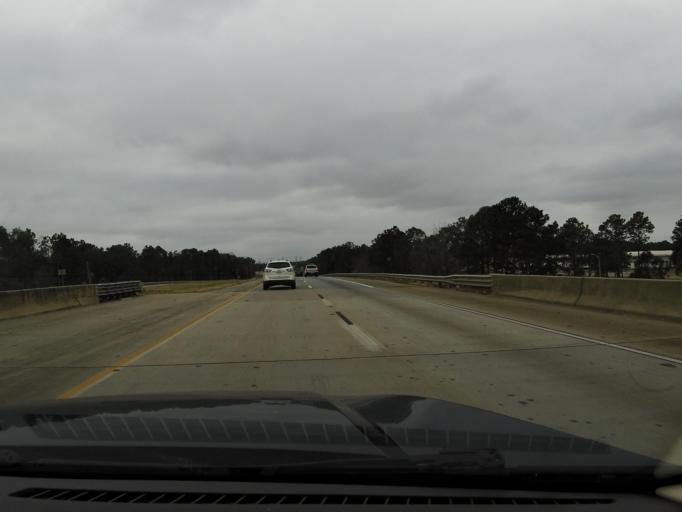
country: US
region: Georgia
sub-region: Dougherty County
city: Albany
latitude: 31.5635
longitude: -84.1136
